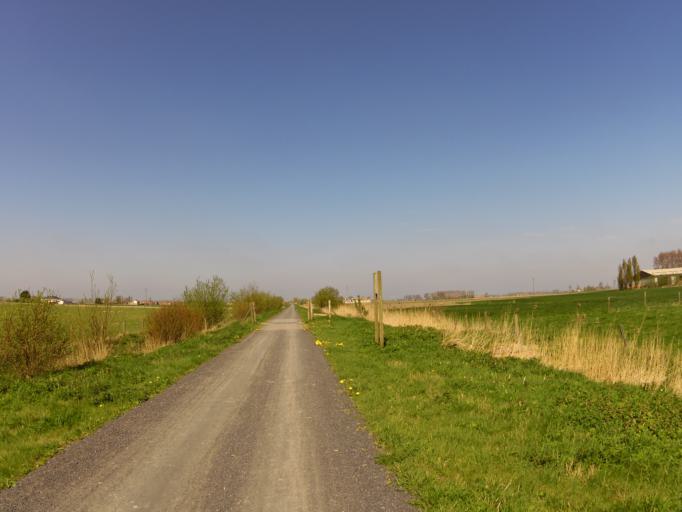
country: BE
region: Flanders
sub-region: Provincie West-Vlaanderen
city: Nieuwpoort
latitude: 51.0848
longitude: 2.7896
